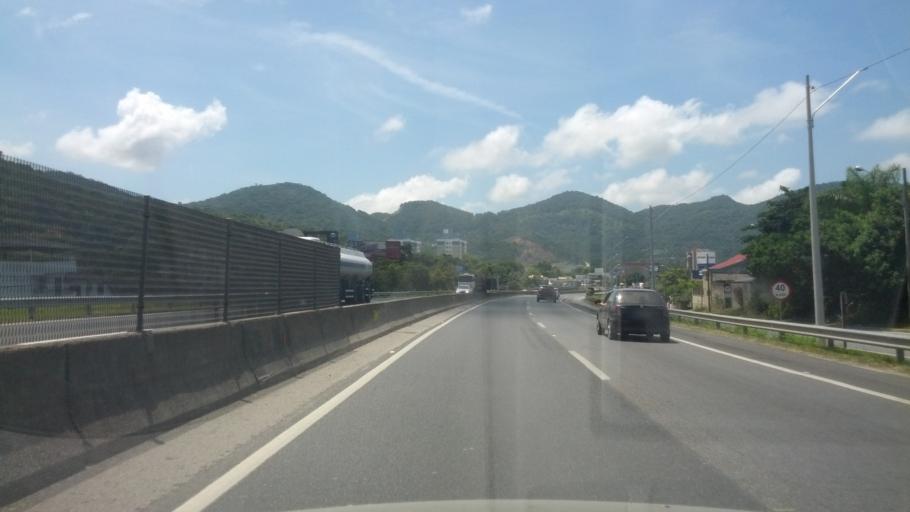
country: BR
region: Santa Catarina
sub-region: Itapema
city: Itapema
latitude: -27.0979
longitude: -48.6187
